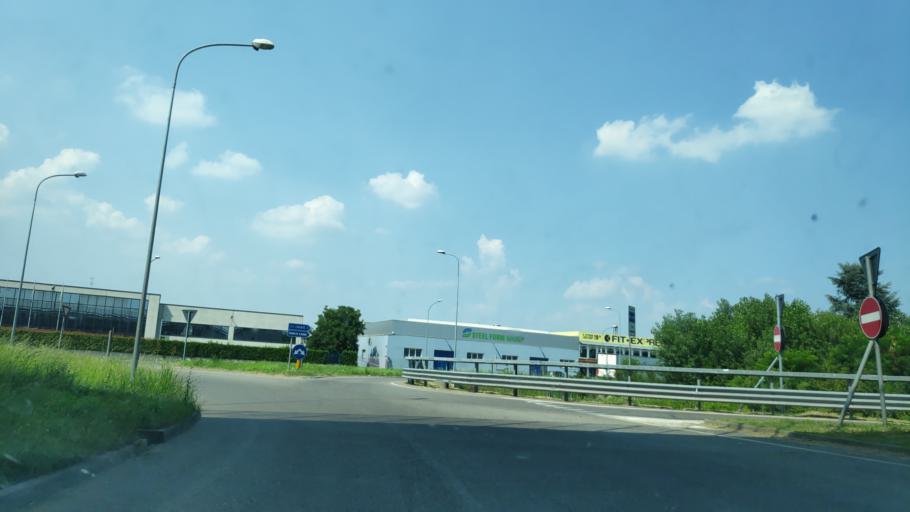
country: IT
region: Lombardy
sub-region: Citta metropolitana di Milano
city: Premenugo
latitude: 45.4831
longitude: 9.3805
